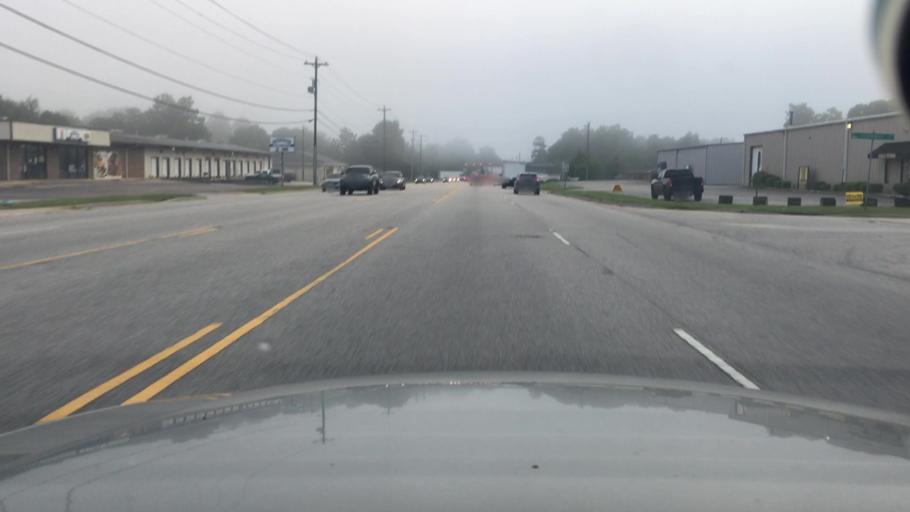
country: US
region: North Carolina
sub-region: Cumberland County
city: Hope Mills
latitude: 35.0150
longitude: -78.9187
